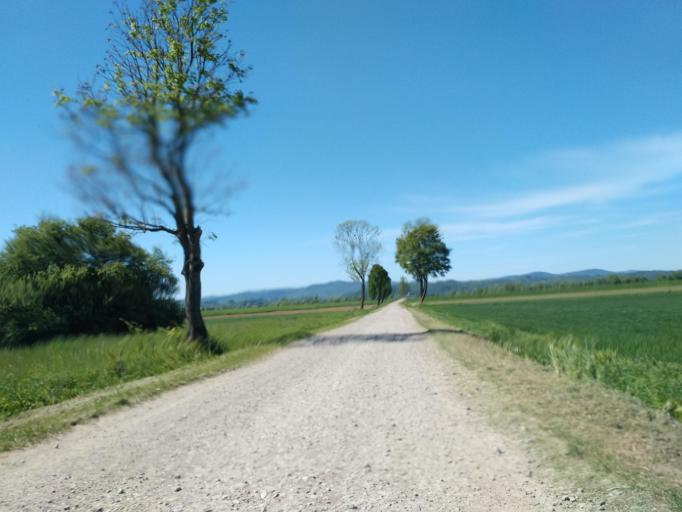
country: PL
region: Subcarpathian Voivodeship
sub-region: Powiat brzozowski
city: Jasionow
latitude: 49.6231
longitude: 21.9777
